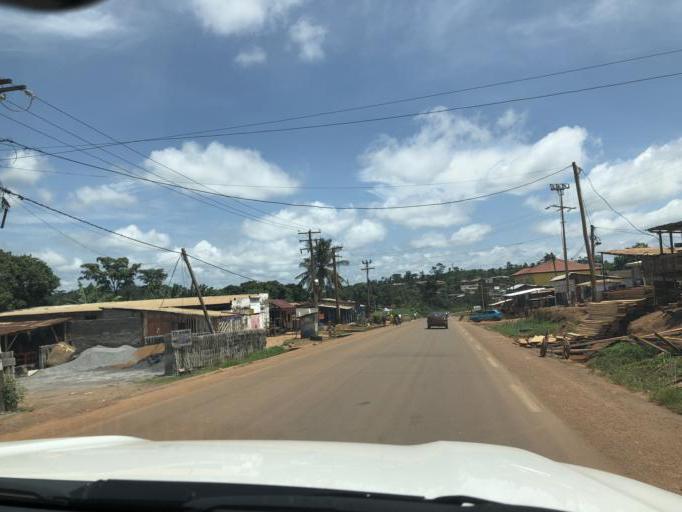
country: CM
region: Centre
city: Yaounde
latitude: 3.8644
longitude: 11.6145
